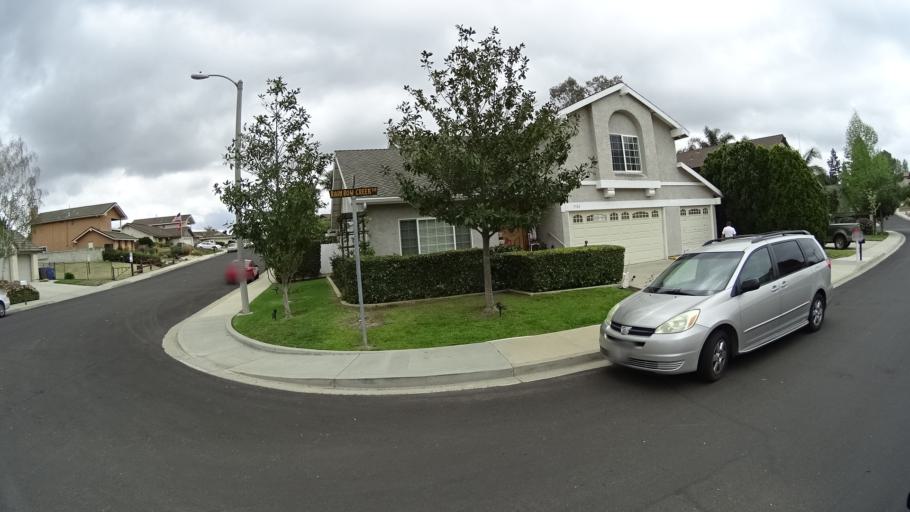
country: US
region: California
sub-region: Ventura County
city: Casa Conejo
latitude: 34.2224
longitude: -118.8961
